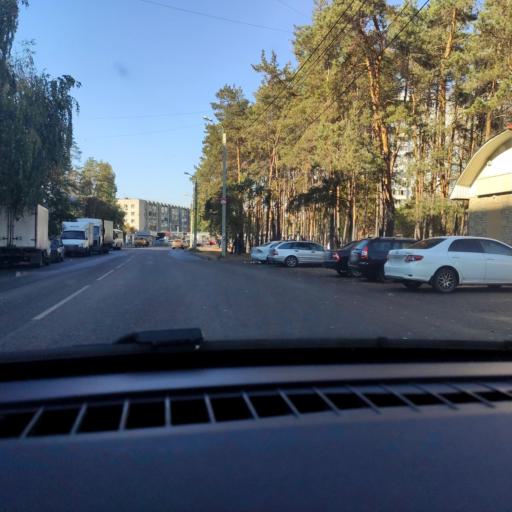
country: RU
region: Voronezj
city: Pridonskoy
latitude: 51.6821
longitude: 39.0870
